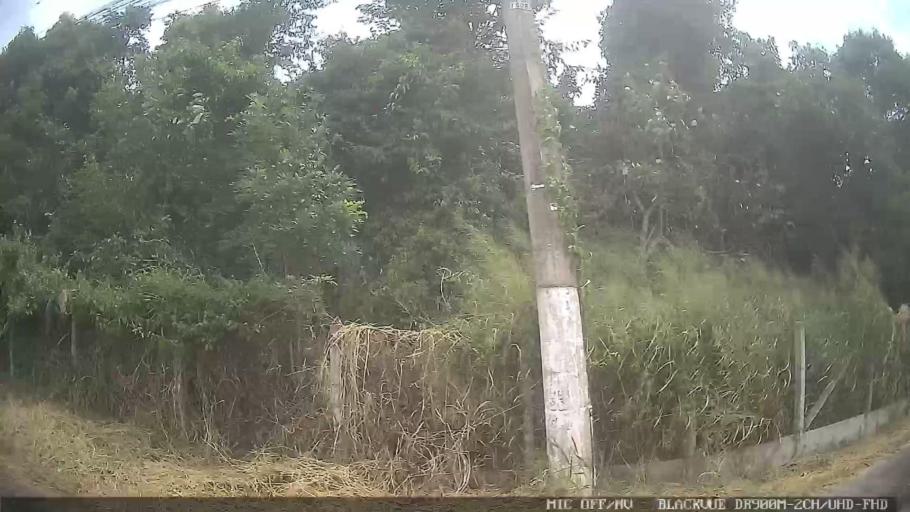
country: BR
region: Sao Paulo
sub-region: Atibaia
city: Atibaia
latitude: -23.0964
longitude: -46.5420
